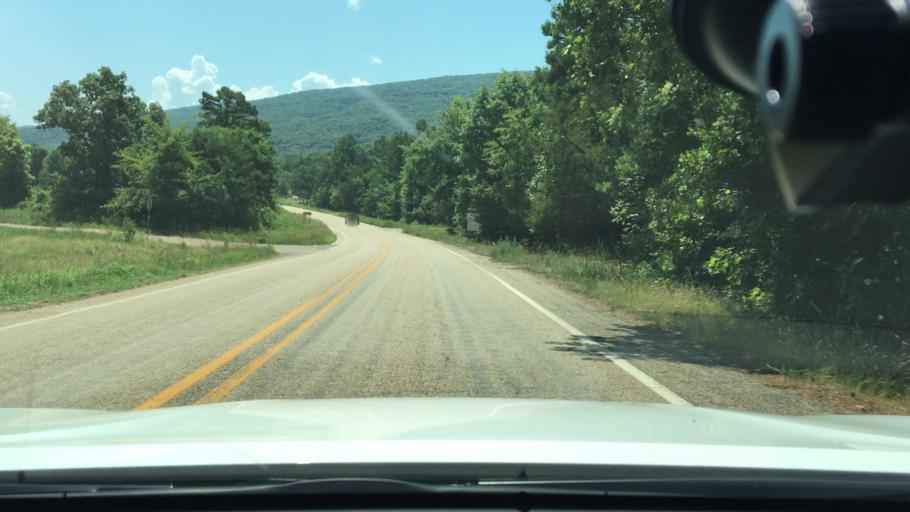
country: US
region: Arkansas
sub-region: Logan County
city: Paris
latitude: 35.1944
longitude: -93.6313
